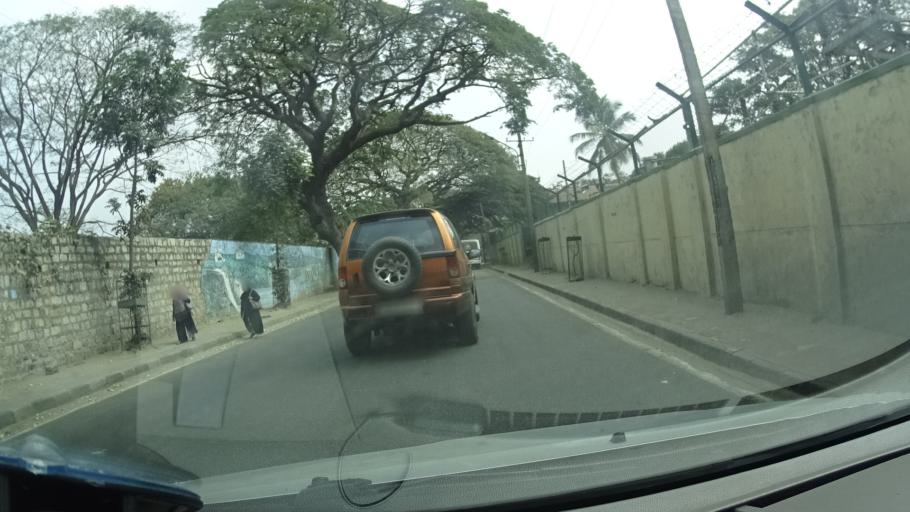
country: IN
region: Karnataka
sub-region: Bangalore Urban
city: Bangalore
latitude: 12.9926
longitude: 77.5992
